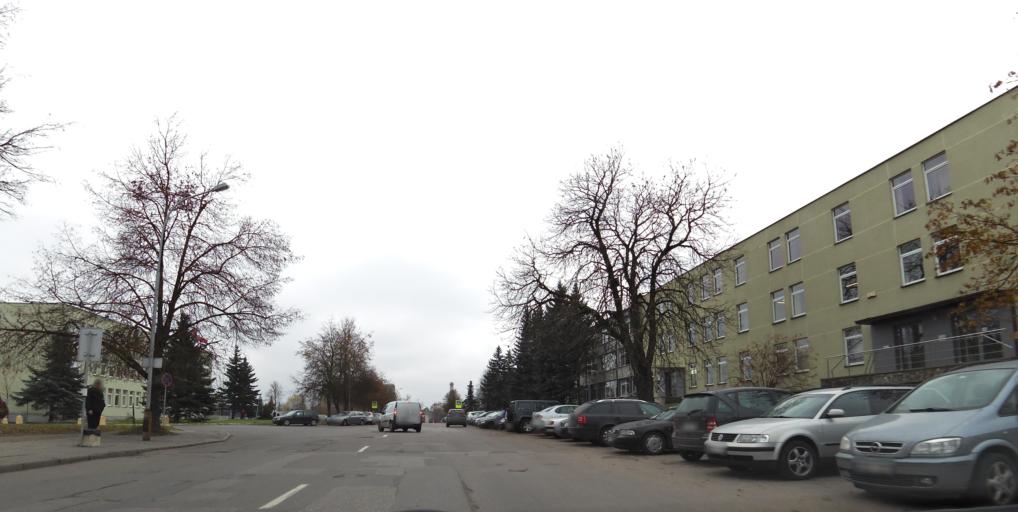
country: LT
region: Vilnius County
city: Vilkpede
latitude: 54.6400
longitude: 25.2667
